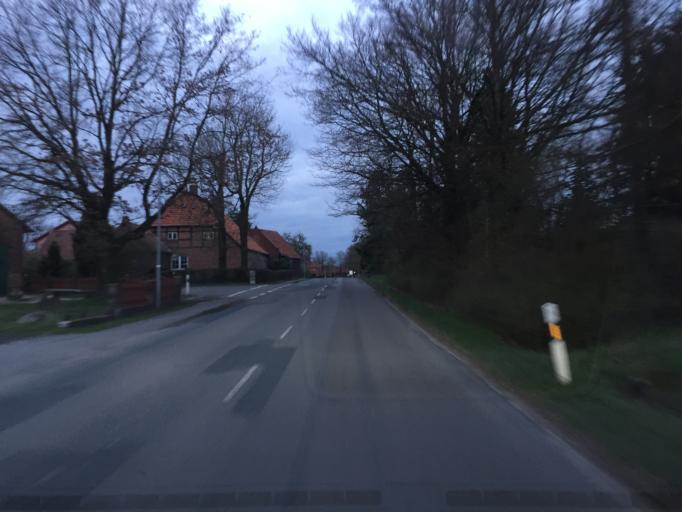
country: DE
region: Lower Saxony
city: Steimbke
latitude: 52.6246
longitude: 9.3909
